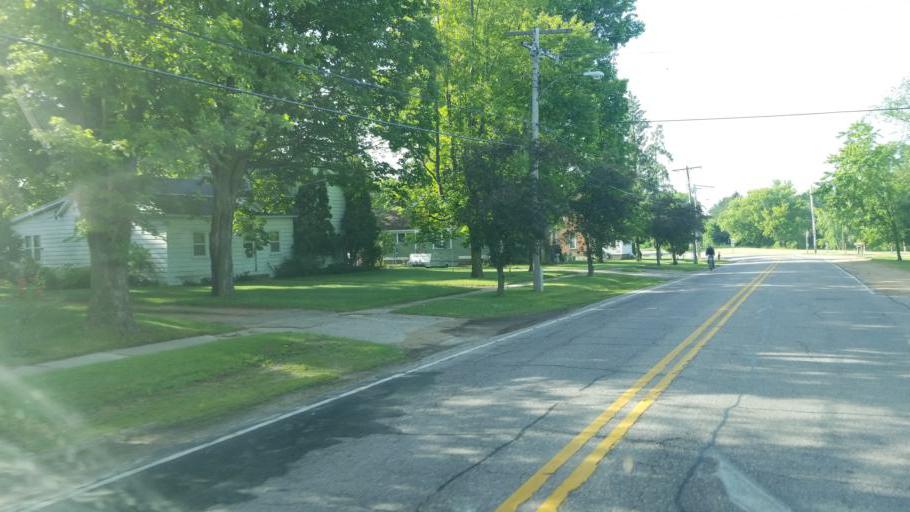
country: US
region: Wisconsin
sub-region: Juneau County
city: Elroy
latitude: 43.6493
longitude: -90.2216
